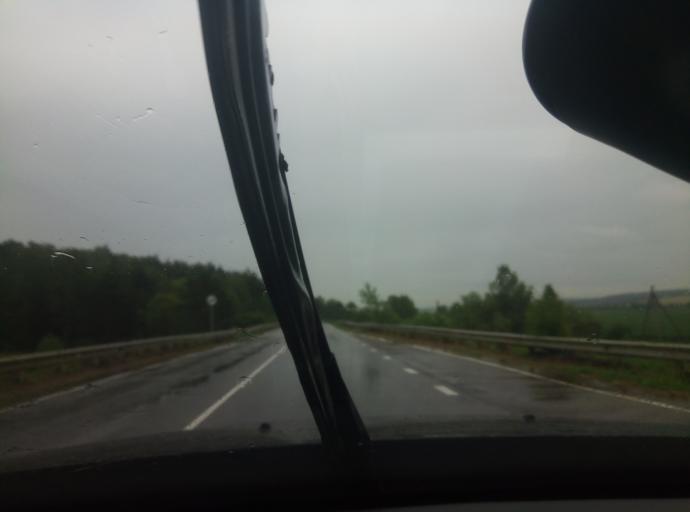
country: RU
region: Kaluga
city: Kremenki
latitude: 54.8948
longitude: 37.0547
